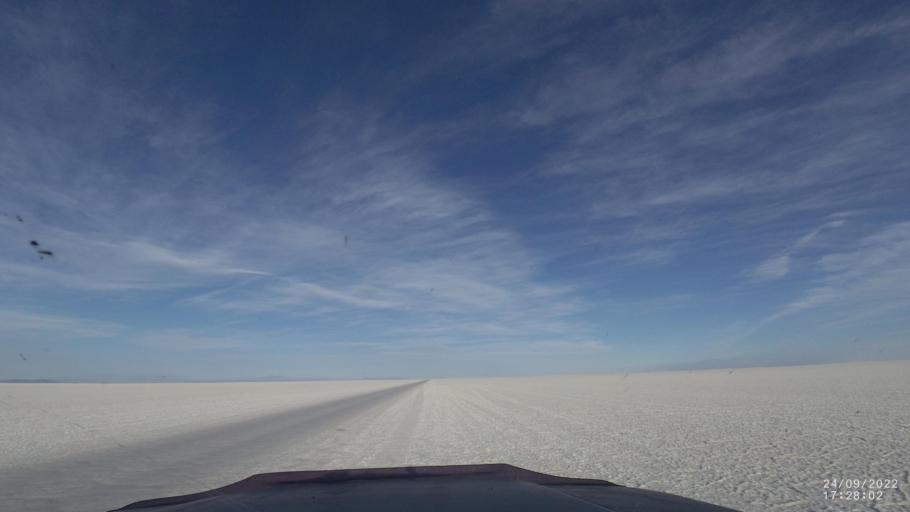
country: BO
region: Potosi
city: Colchani
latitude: -20.3019
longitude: -67.4358
